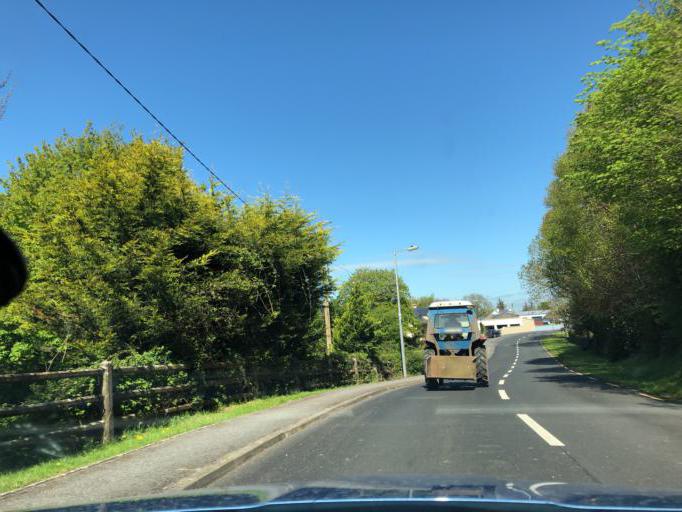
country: IE
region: Connaught
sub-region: County Galway
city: Portumna
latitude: 53.1462
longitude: -8.3711
